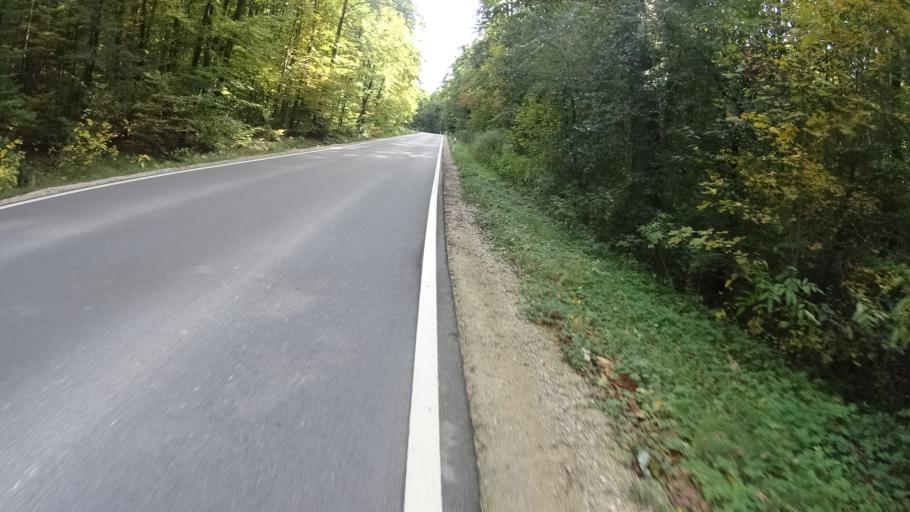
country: DE
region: Bavaria
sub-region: Upper Bavaria
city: Walting
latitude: 48.8985
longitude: 11.3270
